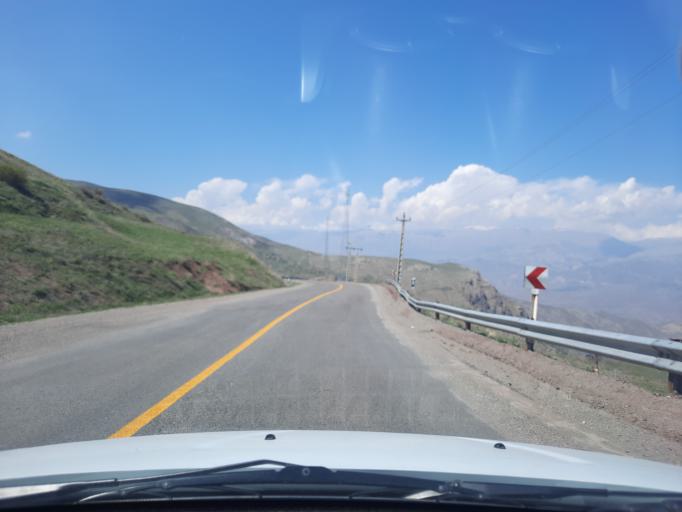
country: IR
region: Qazvin
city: Qazvin
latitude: 36.4043
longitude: 50.2223
